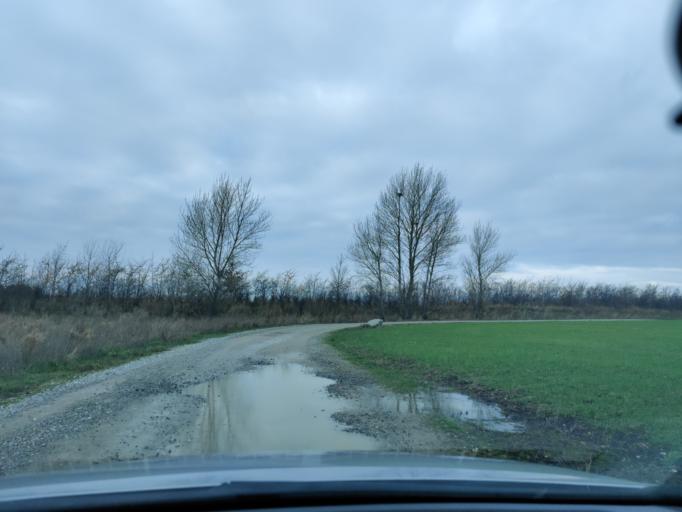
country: DK
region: South Denmark
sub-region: Kerteminde Kommune
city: Kerteminde
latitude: 55.4639
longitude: 10.6546
